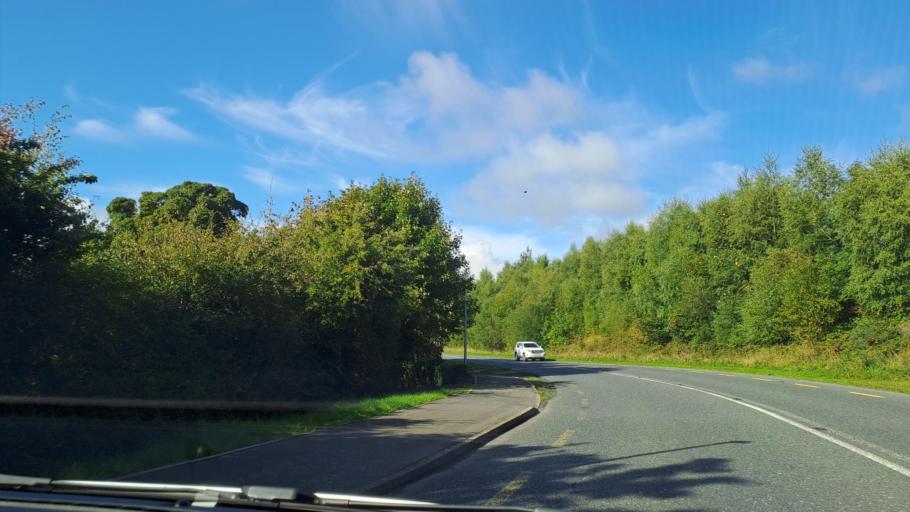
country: IE
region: Ulster
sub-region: County Monaghan
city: Carrickmacross
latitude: 53.9737
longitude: -6.7291
